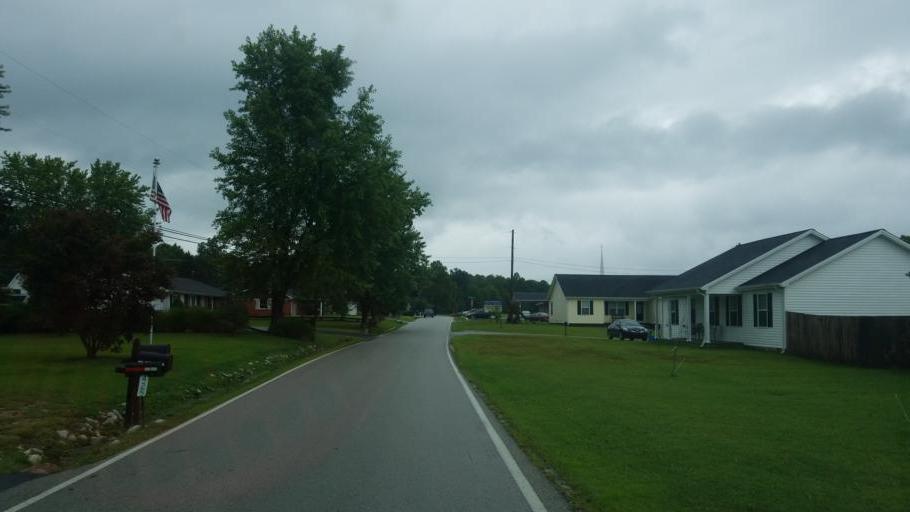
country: US
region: Kentucky
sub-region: Rowan County
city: Morehead
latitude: 38.1524
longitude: -83.5088
